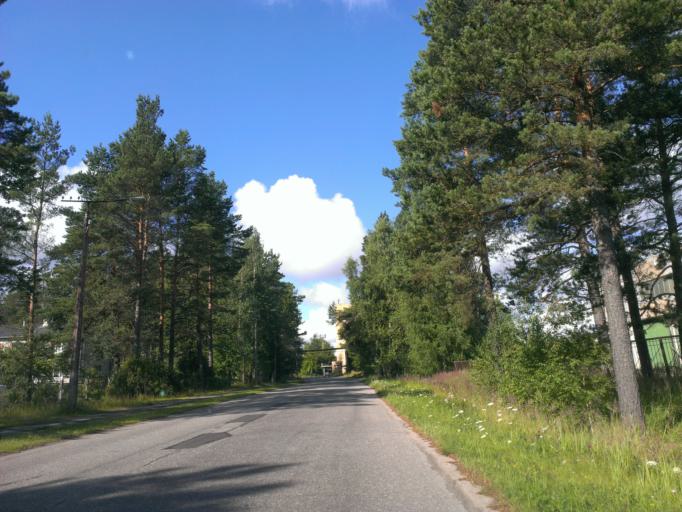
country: LV
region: Incukalns
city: Vangazi
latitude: 57.0896
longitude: 24.5233
